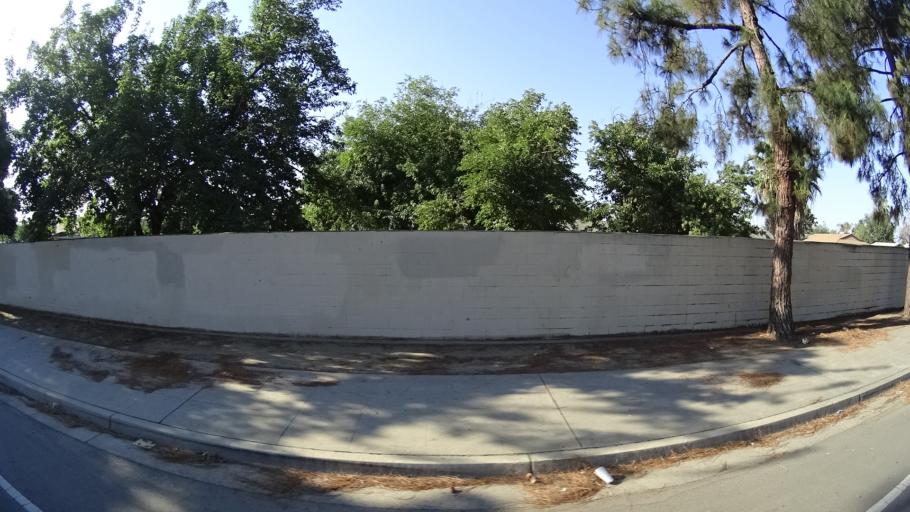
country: US
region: California
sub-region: Fresno County
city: Fresno
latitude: 36.7215
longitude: -119.7979
